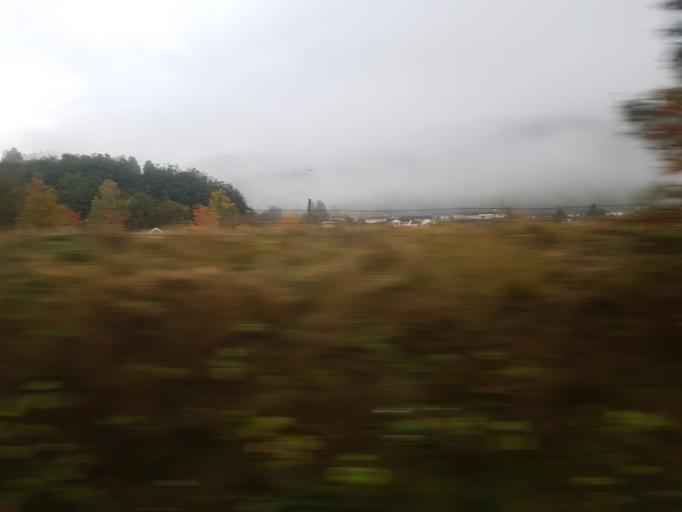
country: NO
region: Sor-Trondelag
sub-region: Melhus
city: Melhus
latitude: 63.2678
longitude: 10.2896
